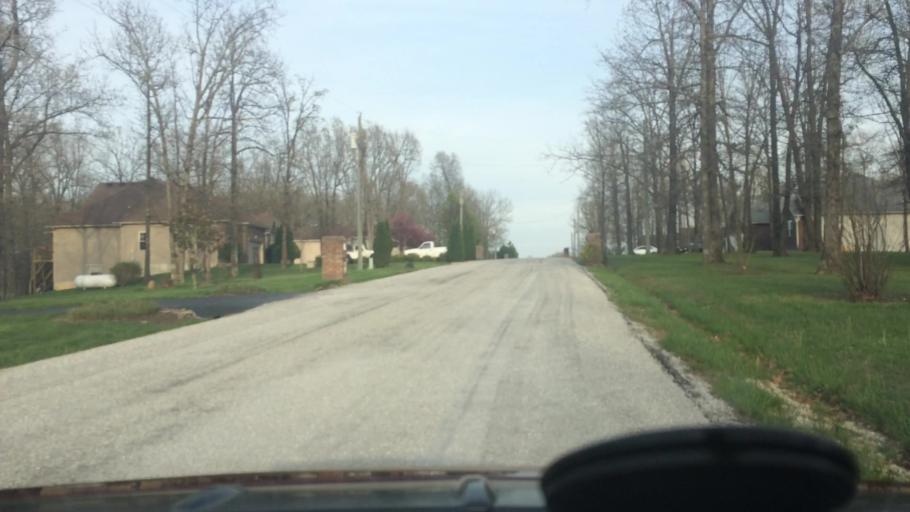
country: US
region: Missouri
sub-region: Greene County
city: Strafford
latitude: 37.2823
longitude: -93.0469
